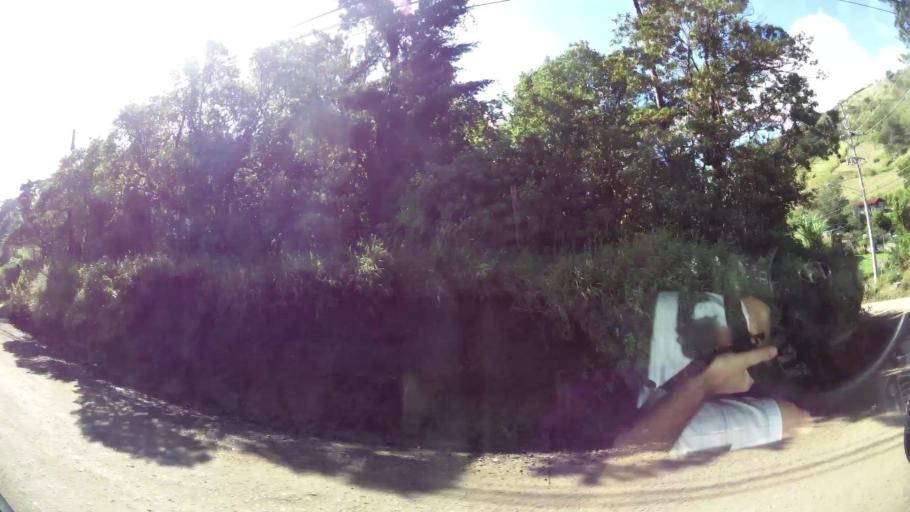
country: CR
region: Guanacaste
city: Juntas
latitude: 10.3291
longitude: -84.8439
